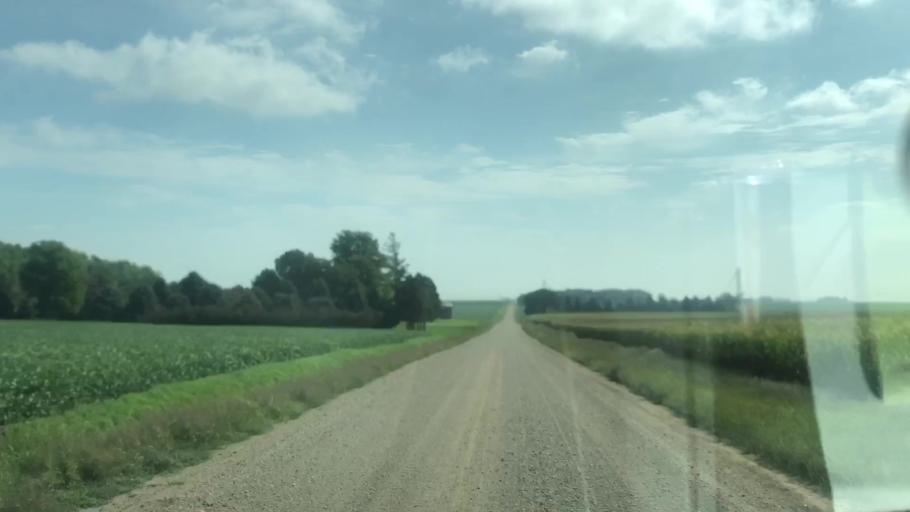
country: US
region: Iowa
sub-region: Lyon County
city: George
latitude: 43.2153
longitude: -95.9912
